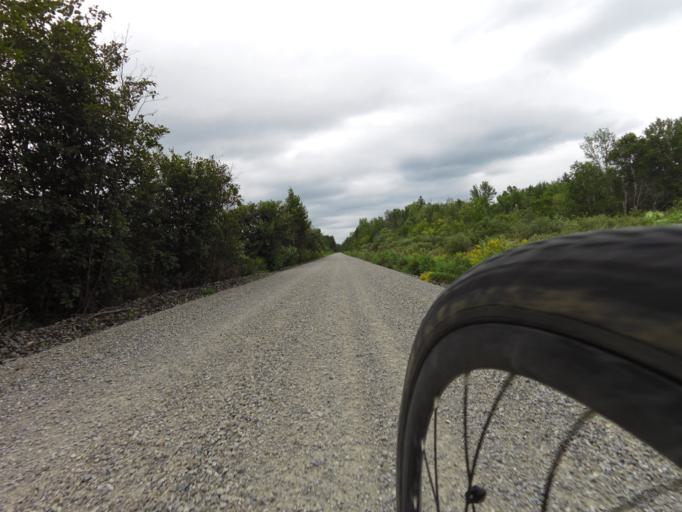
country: CA
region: Ontario
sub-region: Lanark County
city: Smiths Falls
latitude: 44.9561
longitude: -76.0475
